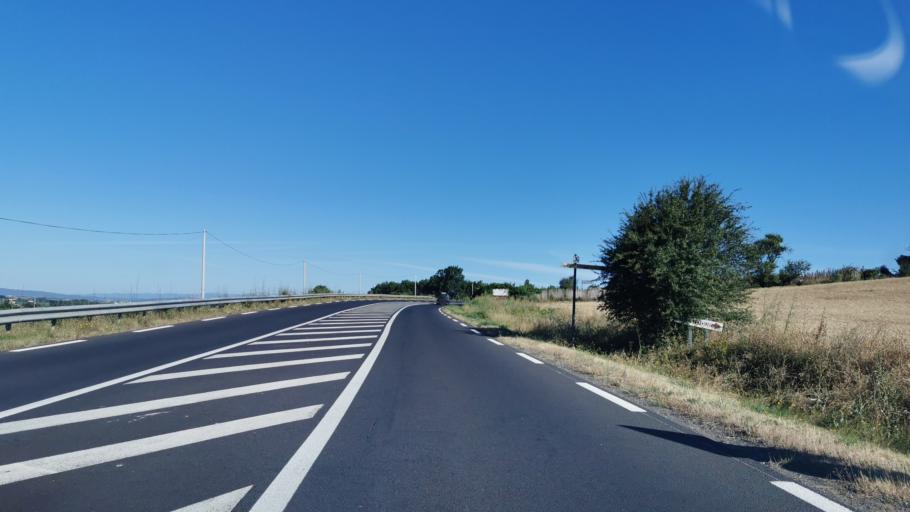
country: FR
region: Languedoc-Roussillon
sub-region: Departement de l'Aude
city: Coursan
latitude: 43.2707
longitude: 3.0795
